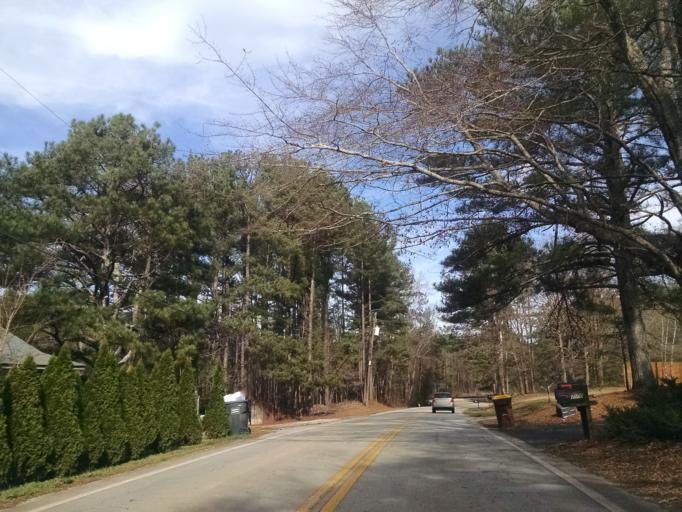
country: US
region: Georgia
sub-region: Gwinnett County
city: Sugar Hill
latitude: 34.0882
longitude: -84.0406
